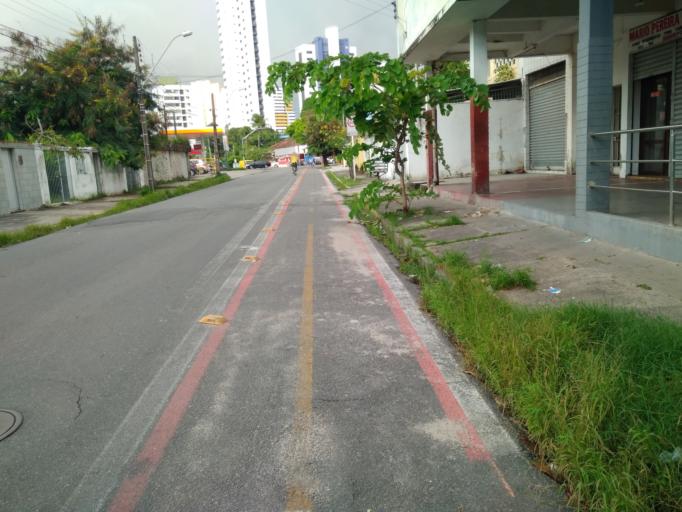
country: BR
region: Pernambuco
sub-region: Recife
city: Recife
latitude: -8.0362
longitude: -34.8921
